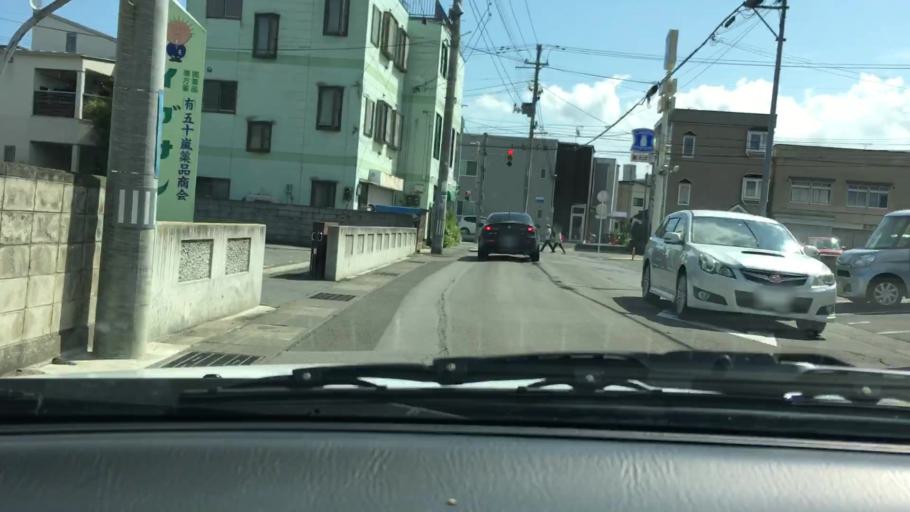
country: JP
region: Aomori
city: Hirosaki
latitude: 40.5953
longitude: 140.4730
